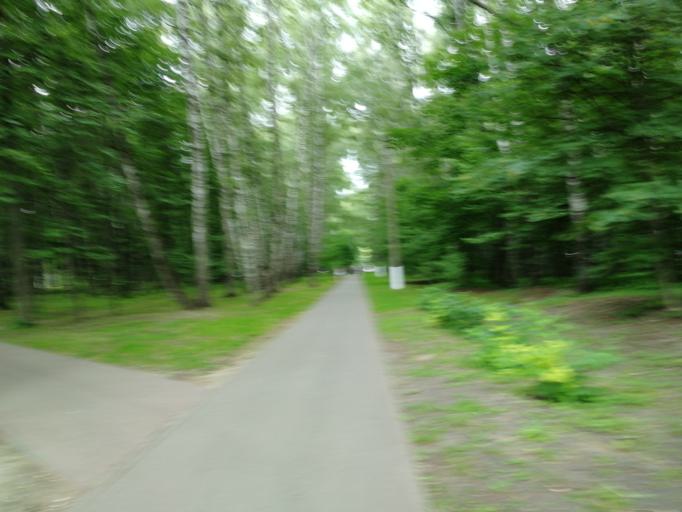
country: RU
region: Tula
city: Tula
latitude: 54.1815
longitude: 37.5899
